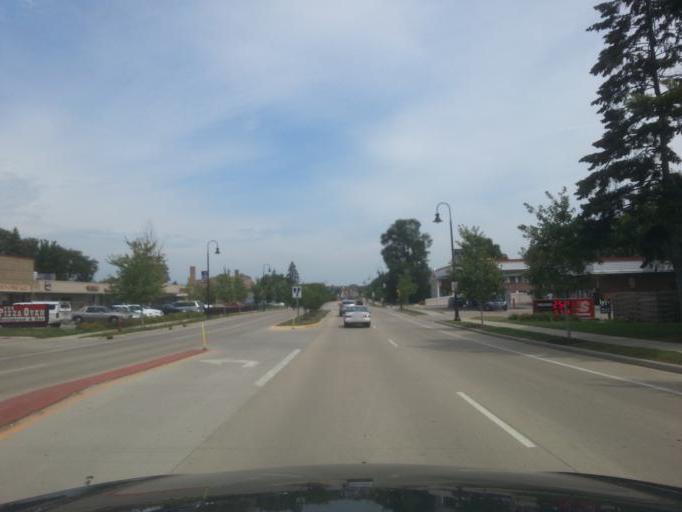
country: US
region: Wisconsin
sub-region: Dane County
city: Monona
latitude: 43.0595
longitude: -89.3259
